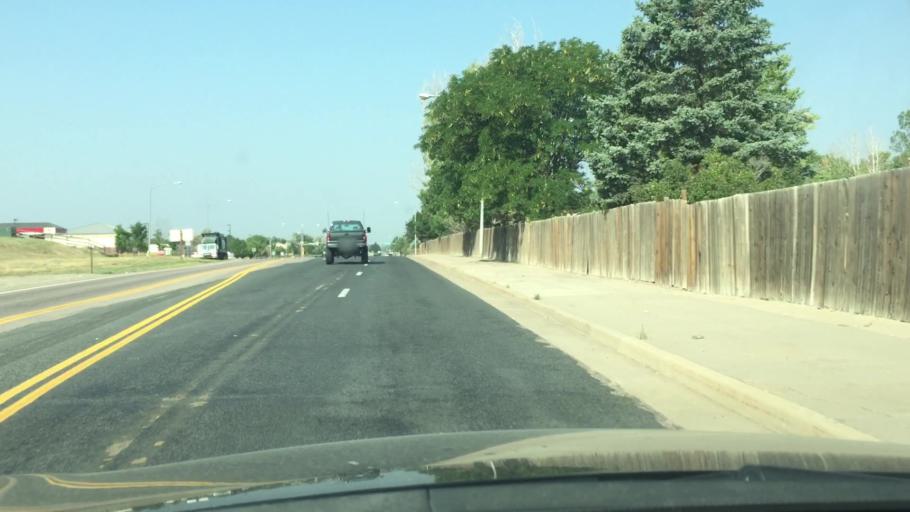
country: US
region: Colorado
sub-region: Arapahoe County
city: Dove Valley
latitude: 39.6386
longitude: -104.7593
